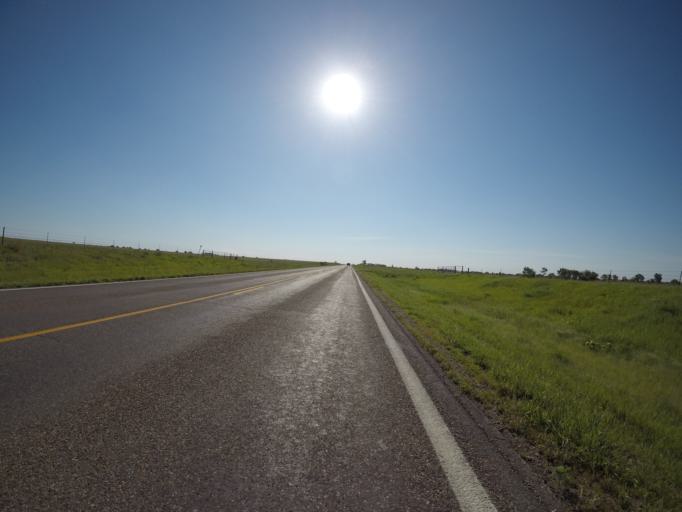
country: US
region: Kansas
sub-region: Lyon County
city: Emporia
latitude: 38.6588
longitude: -96.2161
